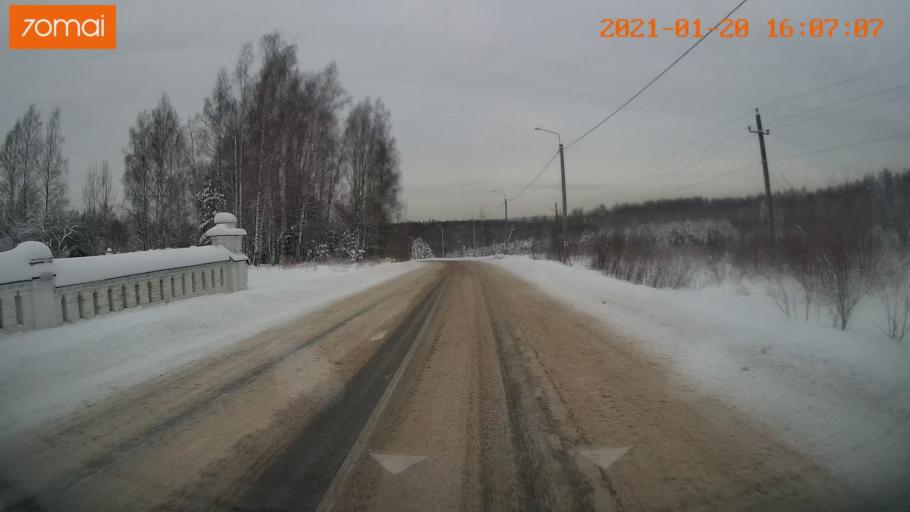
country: RU
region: Vladimir
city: Sudogda
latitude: 56.0736
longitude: 40.7857
